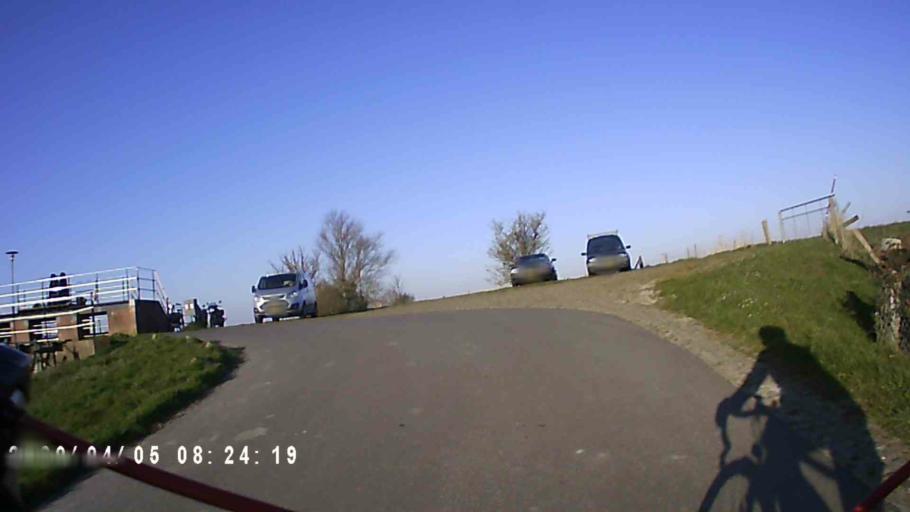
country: NL
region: Groningen
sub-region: Gemeente Winsum
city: Winsum
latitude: 53.3291
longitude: 6.4634
